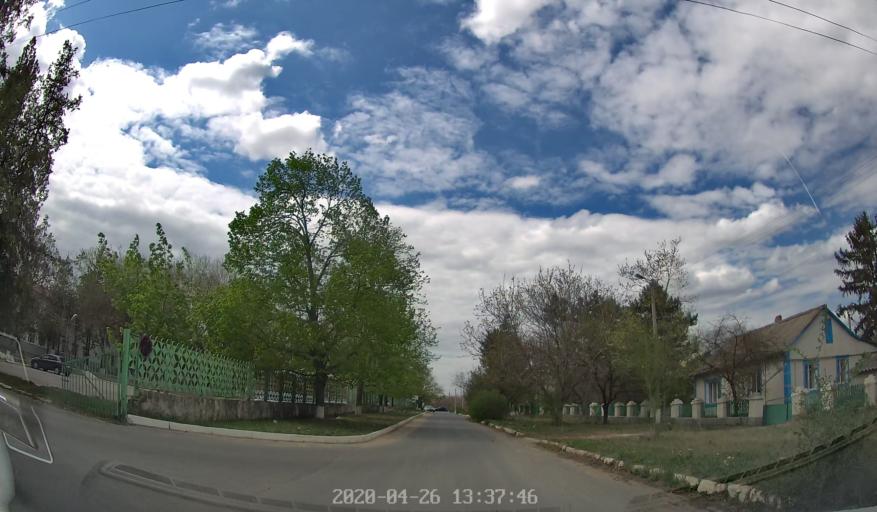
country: MD
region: Criuleni
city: Criuleni
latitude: 47.2062
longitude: 29.1690
